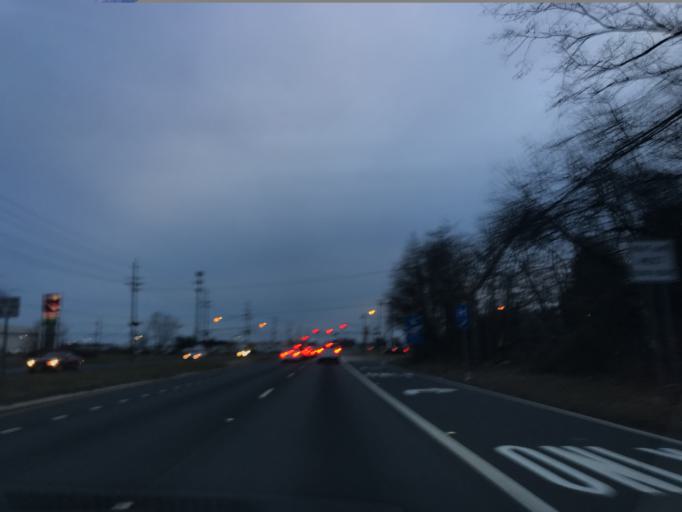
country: US
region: New Jersey
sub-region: Middlesex County
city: Dayton
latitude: 40.3808
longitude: -74.5022
